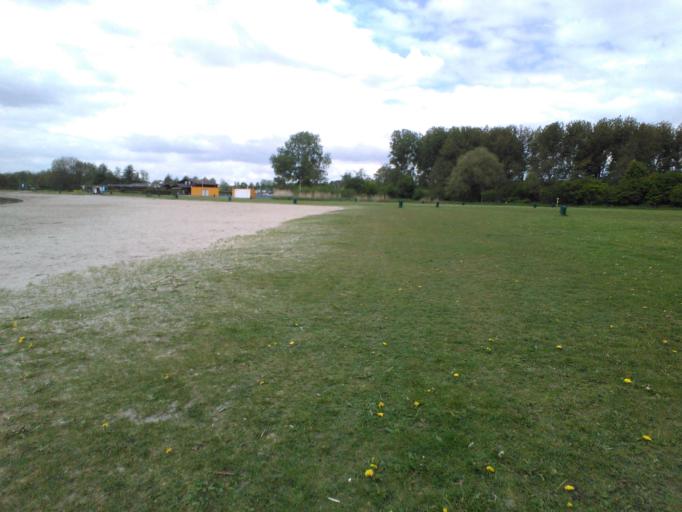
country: NL
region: South Holland
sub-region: Bodegraven-Reeuwijk
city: Reeuwijk
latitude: 52.0594
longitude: 4.7427
